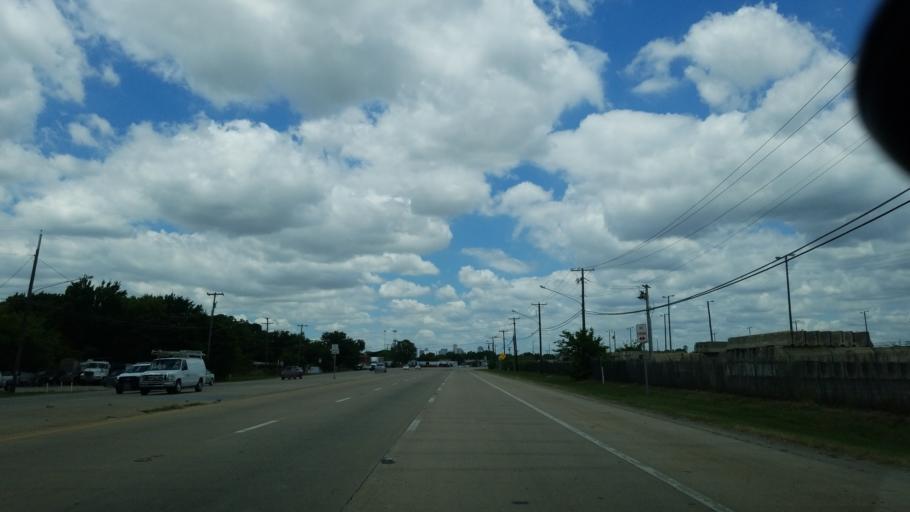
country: US
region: Texas
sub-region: Dallas County
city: Hutchins
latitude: 32.7174
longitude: -96.7563
